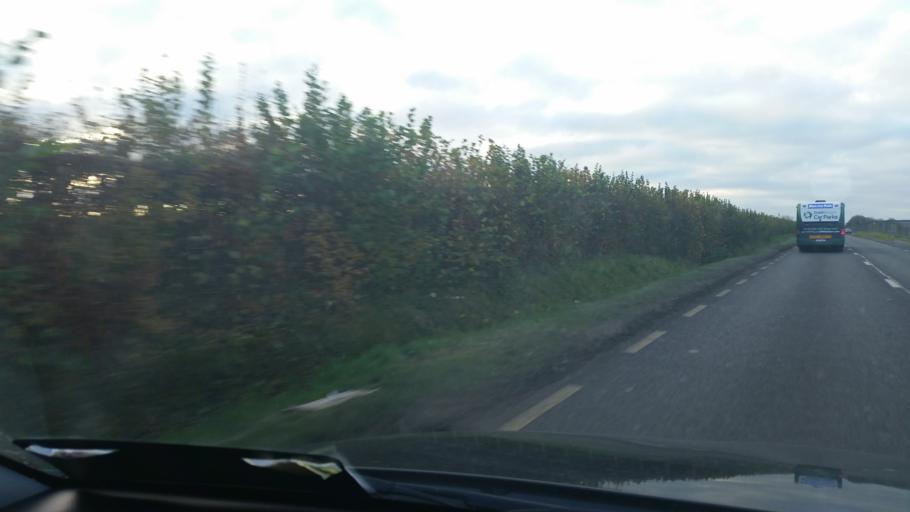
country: IE
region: Leinster
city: Beaumont
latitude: 53.4177
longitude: -6.2422
